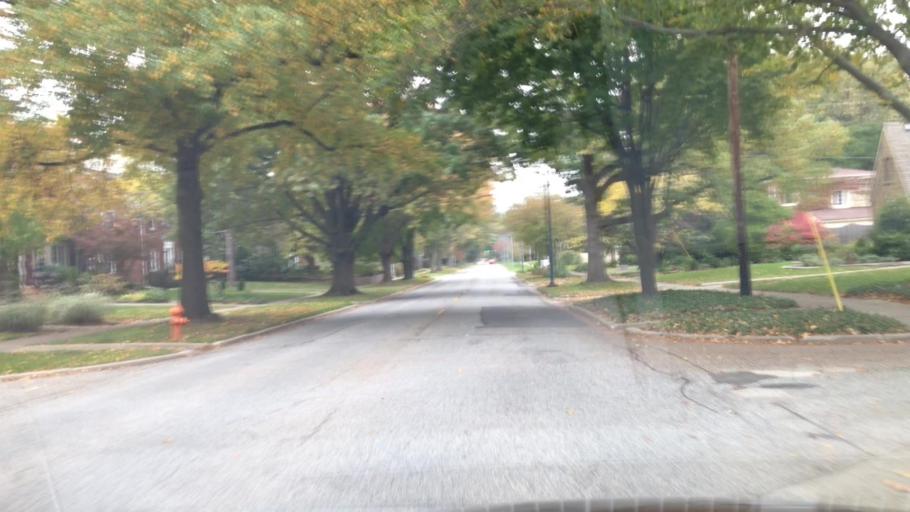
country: US
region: Illinois
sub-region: Champaign County
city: Champaign
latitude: 40.1101
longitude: -88.2627
